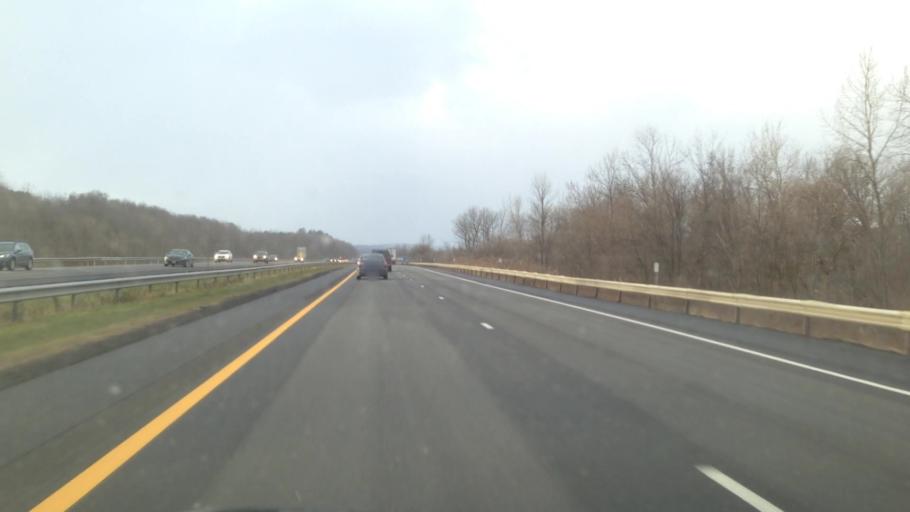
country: US
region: New York
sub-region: Montgomery County
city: Tribes Hill
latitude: 42.9346
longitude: -74.3227
